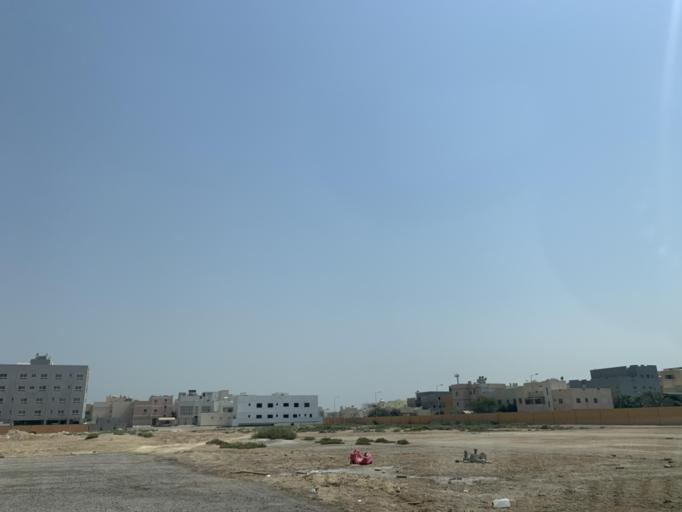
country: BH
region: Manama
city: Jidd Hafs
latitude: 26.2111
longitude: 50.5235
